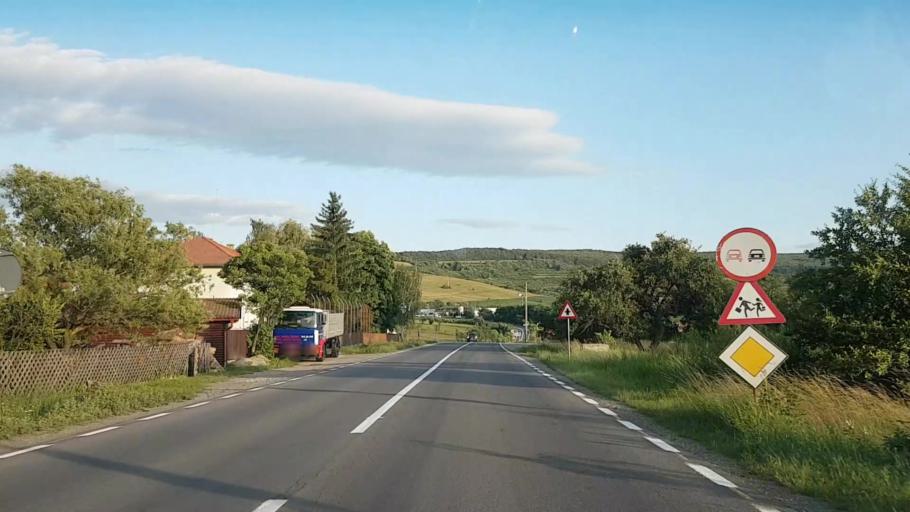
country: RO
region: Harghita
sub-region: Comuna Lupeni
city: Lupeni
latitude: 46.3609
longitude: 25.2378
